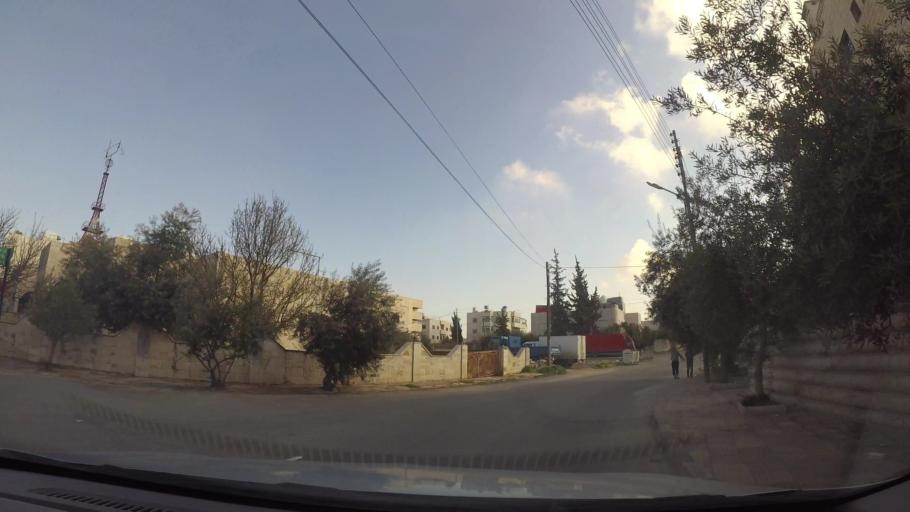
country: JO
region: Amman
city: Al Bunayyat ash Shamaliyah
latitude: 31.9006
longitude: 35.9168
